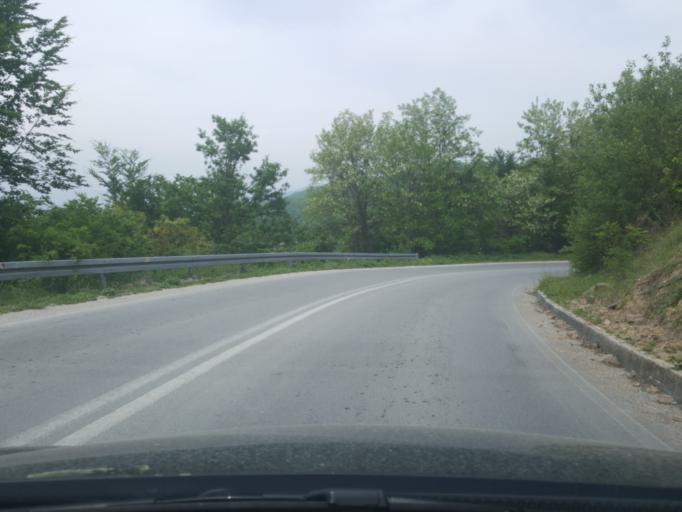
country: RS
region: Central Serbia
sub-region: Zlatiborski Okrug
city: Bajina Basta
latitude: 43.9258
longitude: 19.5659
